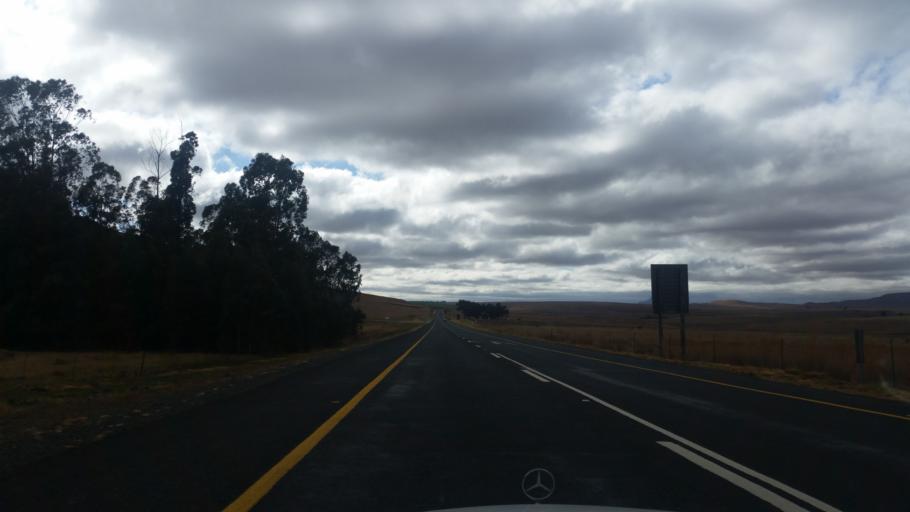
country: ZA
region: Orange Free State
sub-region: Thabo Mofutsanyana District Municipality
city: Phuthaditjhaba
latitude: -28.3126
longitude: 28.7493
